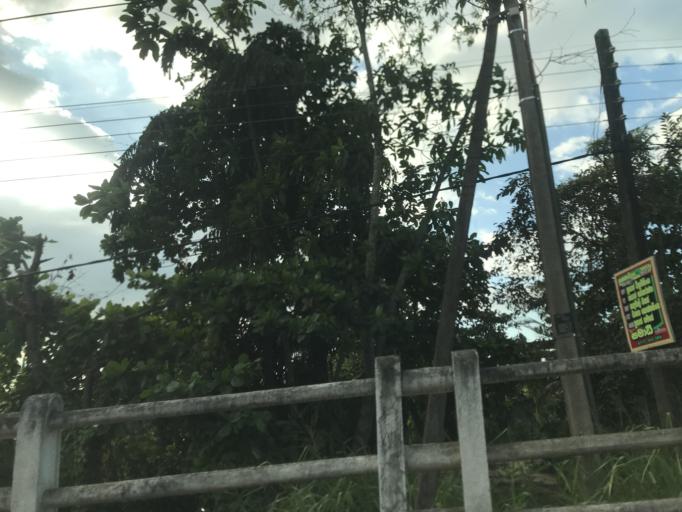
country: LK
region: Western
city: Gampaha
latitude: 7.0830
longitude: 79.9867
